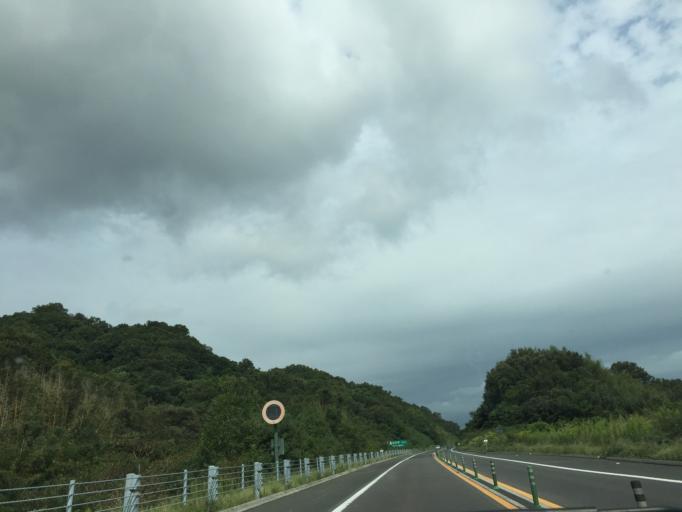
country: JP
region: Kagawa
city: Shido
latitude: 34.2595
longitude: 134.2884
